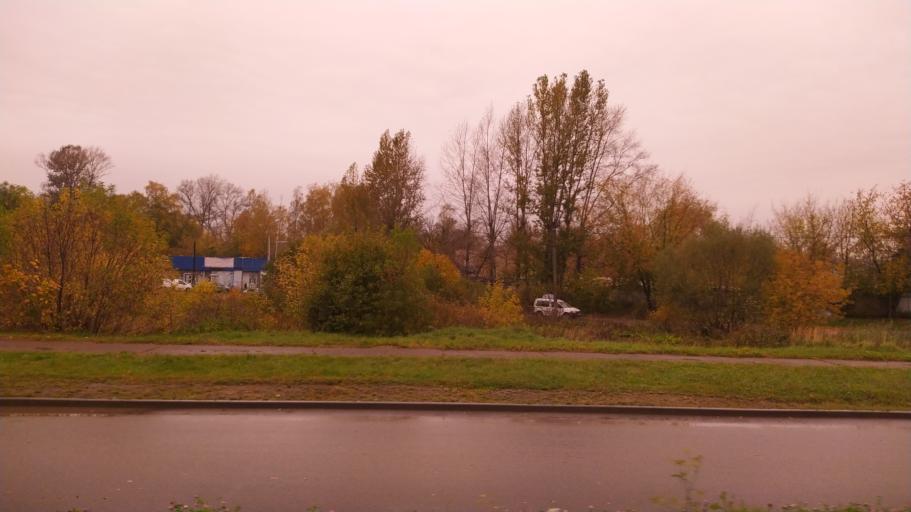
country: RU
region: Tverskaya
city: Tver
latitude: 56.8300
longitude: 35.8994
